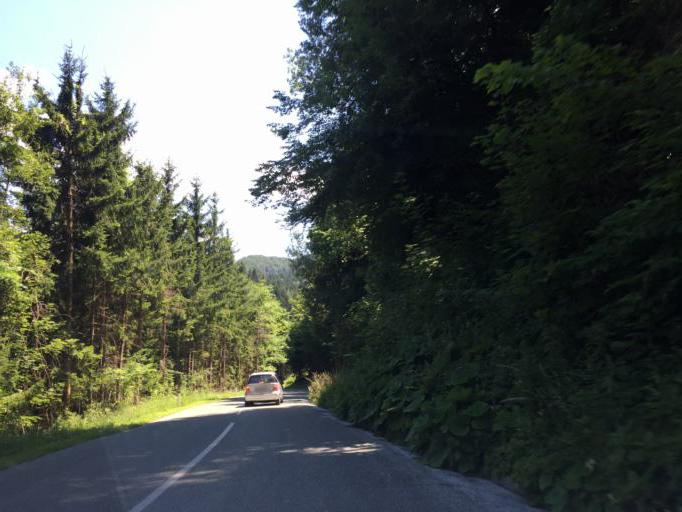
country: SI
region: Gorje
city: Zgornje Gorje
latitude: 46.3741
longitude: 14.0435
